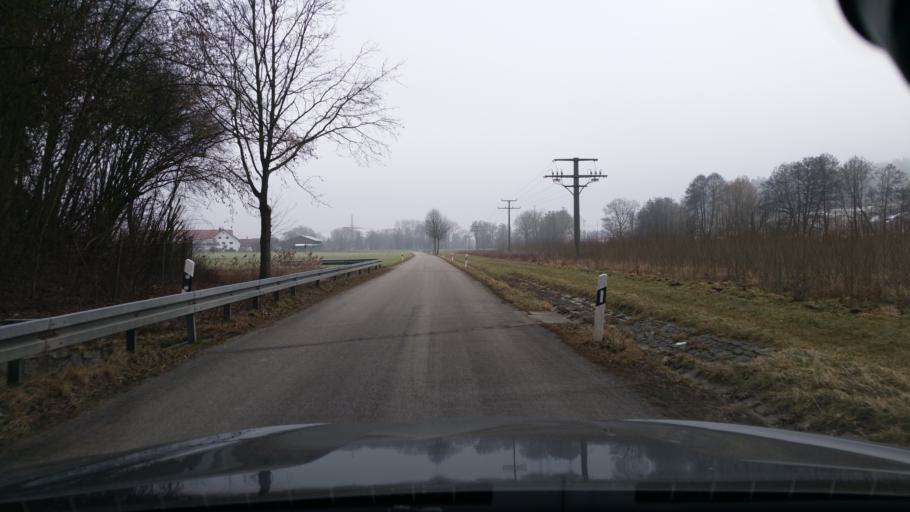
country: DE
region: Bavaria
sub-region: Lower Bavaria
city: Weihmichl
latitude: 48.5649
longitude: 12.0892
